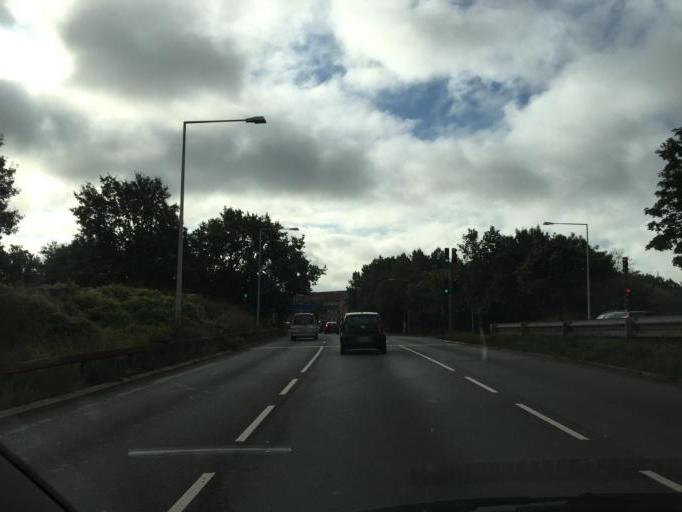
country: DK
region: Capital Region
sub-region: Frederiksberg Kommune
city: Frederiksberg
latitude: 55.7034
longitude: 12.5177
